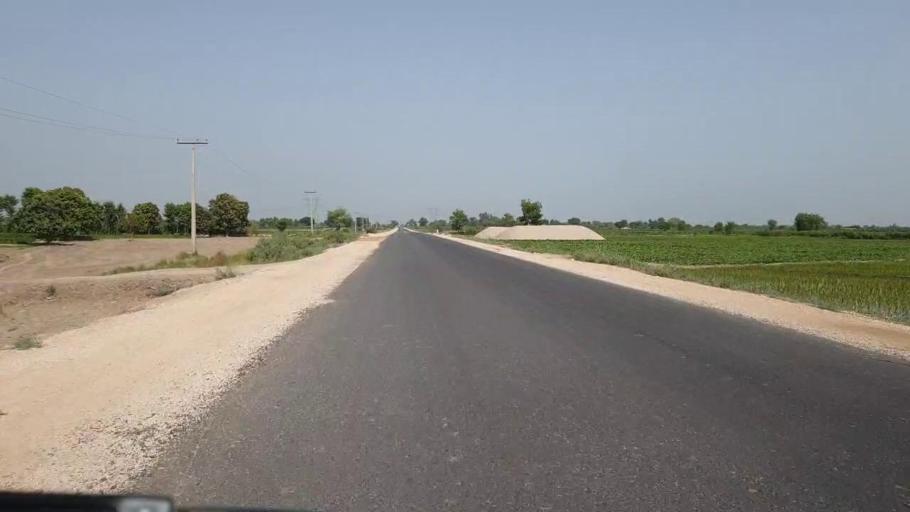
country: PK
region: Sindh
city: Sakrand
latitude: 26.2570
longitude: 68.1934
